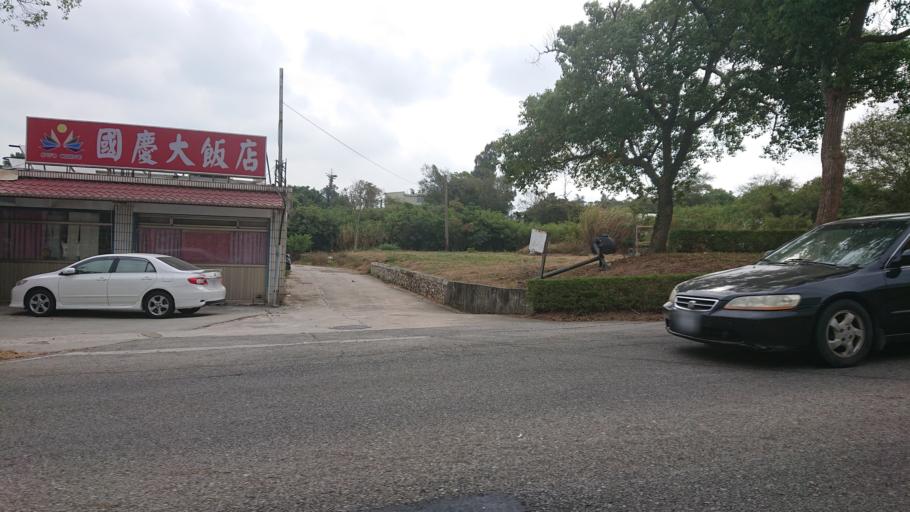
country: TW
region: Fukien
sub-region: Kinmen
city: Jincheng
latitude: 24.4274
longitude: 118.3214
